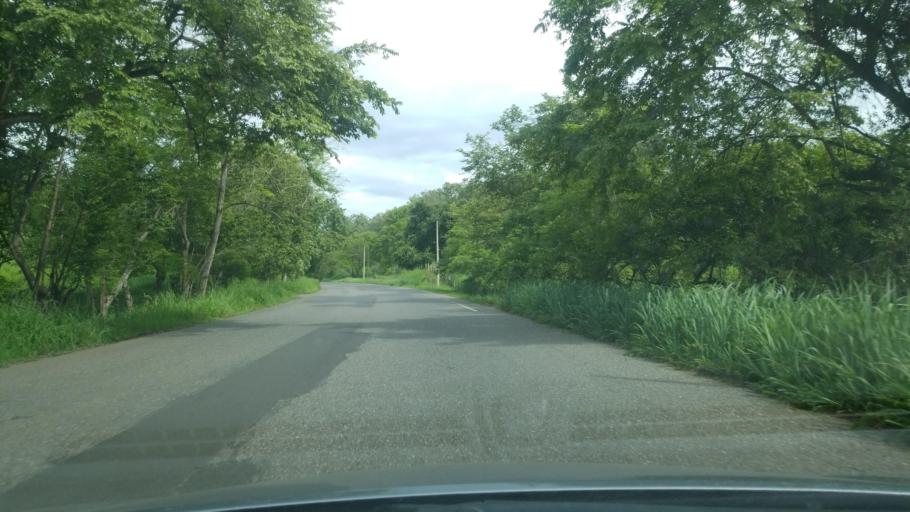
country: HN
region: Santa Barbara
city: Camalote
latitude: 15.3405
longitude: -88.3585
